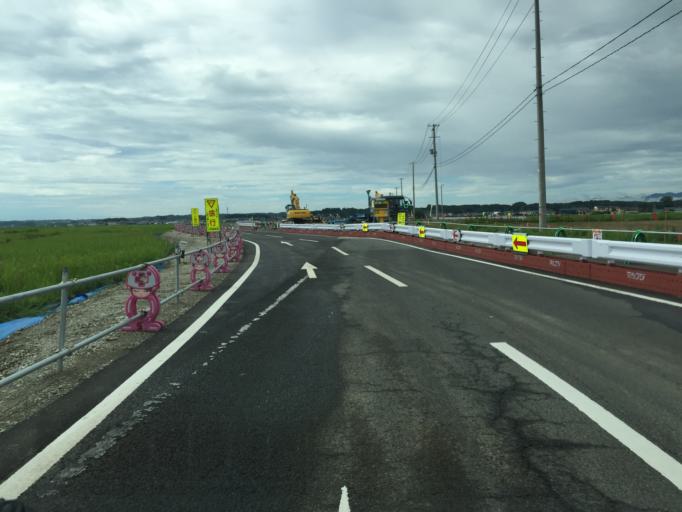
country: JP
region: Miyagi
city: Marumori
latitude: 37.7969
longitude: 140.9568
